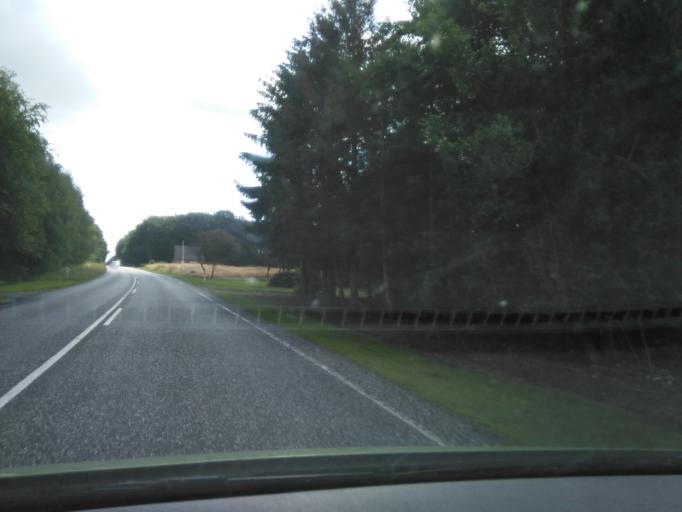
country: DK
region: Central Jutland
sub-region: Arhus Kommune
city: Solbjerg
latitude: 55.9701
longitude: 10.0712
